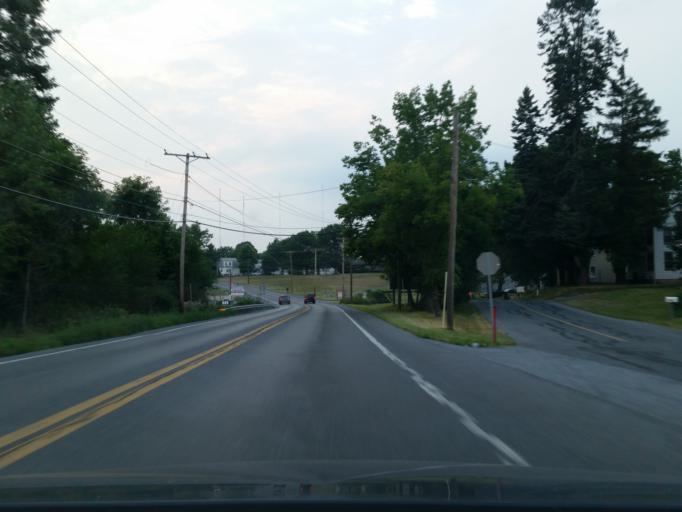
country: US
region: Pennsylvania
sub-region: Lebanon County
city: Pleasant Hill
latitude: 40.3548
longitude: -76.4554
